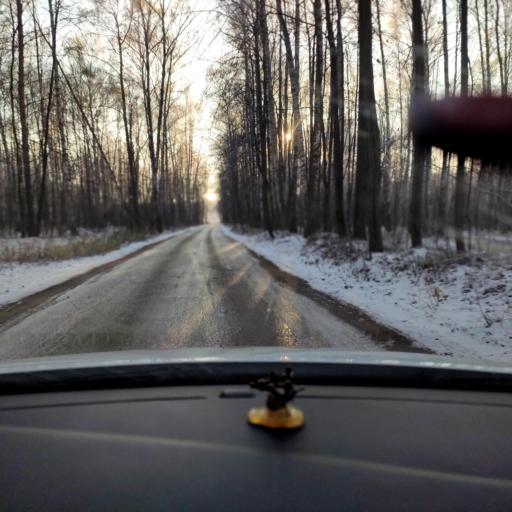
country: RU
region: Tatarstan
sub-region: Gorod Kazan'
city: Kazan
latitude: 55.6751
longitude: 49.1029
